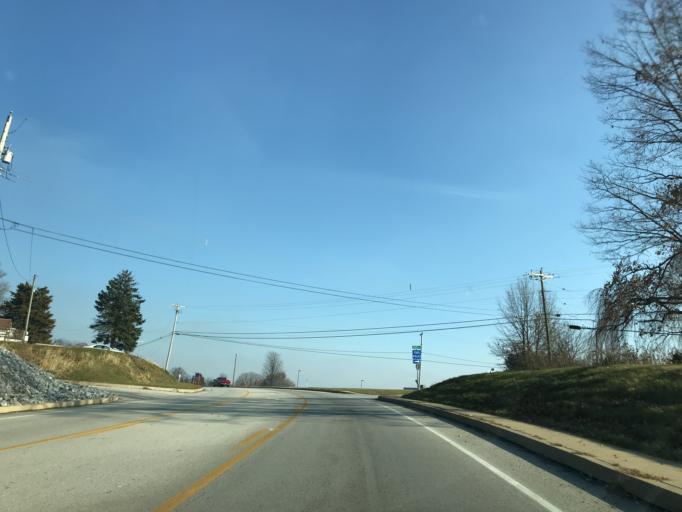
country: US
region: Pennsylvania
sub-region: York County
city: Loganville
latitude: 39.8641
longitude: -76.7023
